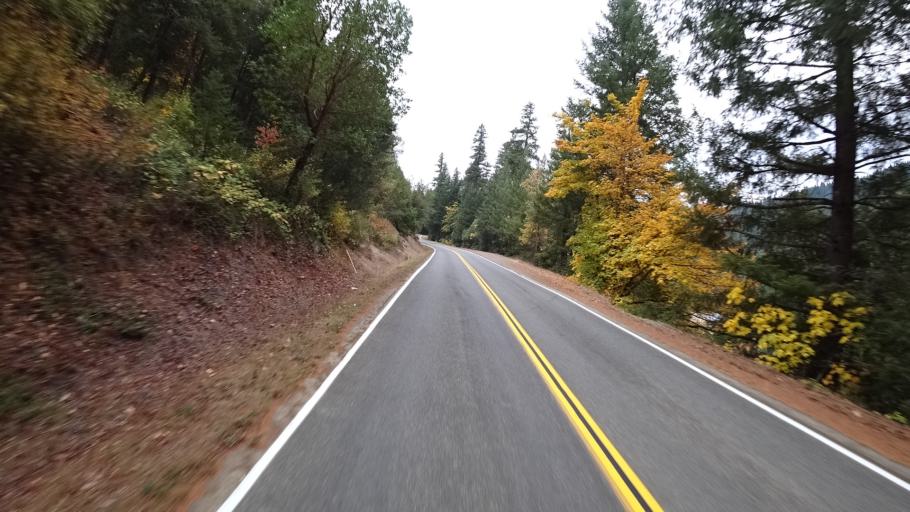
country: US
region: California
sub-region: Siskiyou County
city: Happy Camp
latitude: 41.8171
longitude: -123.3815
